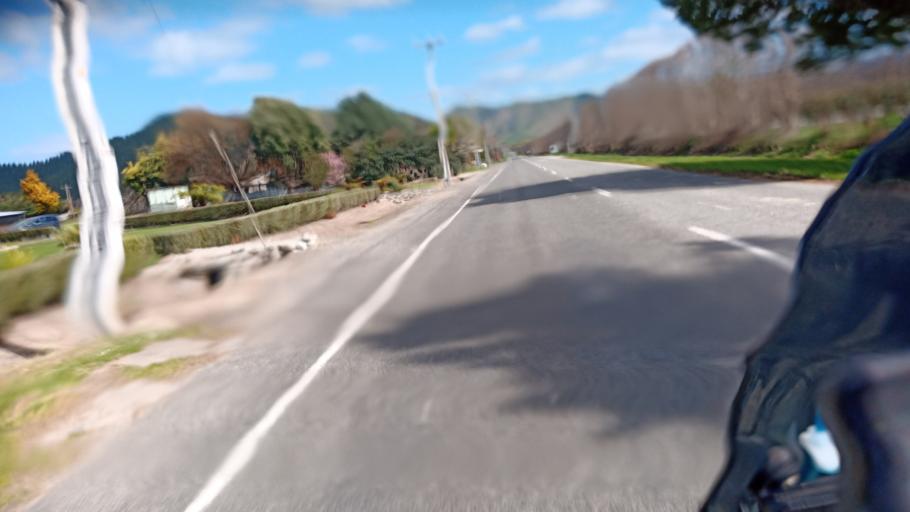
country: NZ
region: Gisborne
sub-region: Gisborne District
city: Gisborne
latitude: -38.6799
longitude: 177.9017
